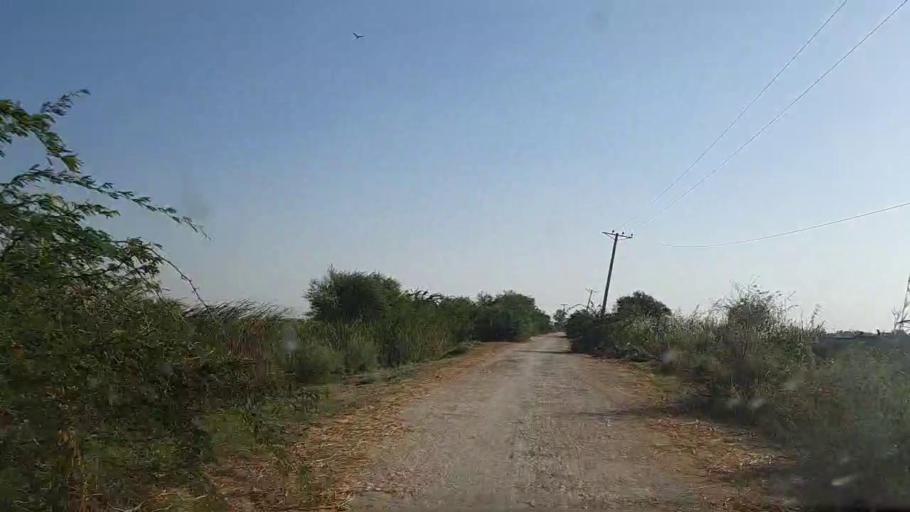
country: PK
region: Sindh
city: Thatta
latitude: 24.6371
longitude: 68.0763
